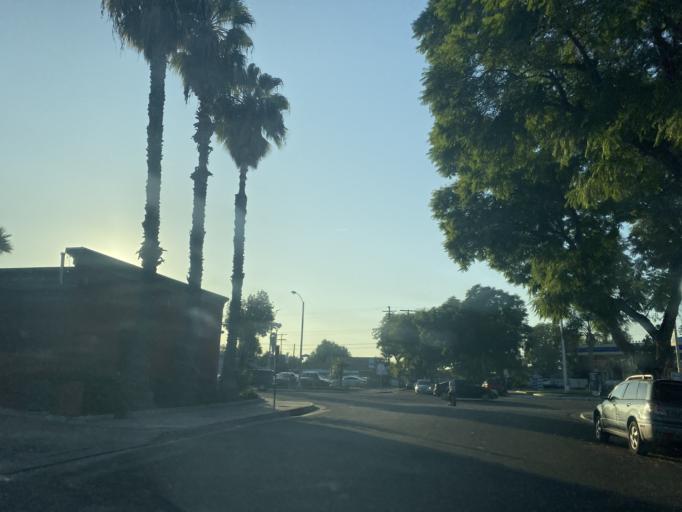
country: US
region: California
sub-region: Orange County
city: Fullerton
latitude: 33.8652
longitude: -117.9238
